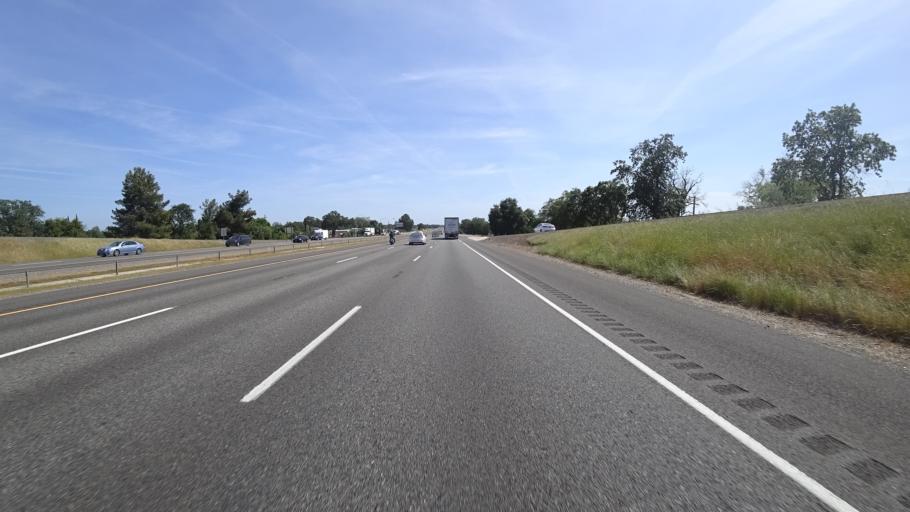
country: US
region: California
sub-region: Shasta County
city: Redding
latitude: 40.5368
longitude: -122.3507
